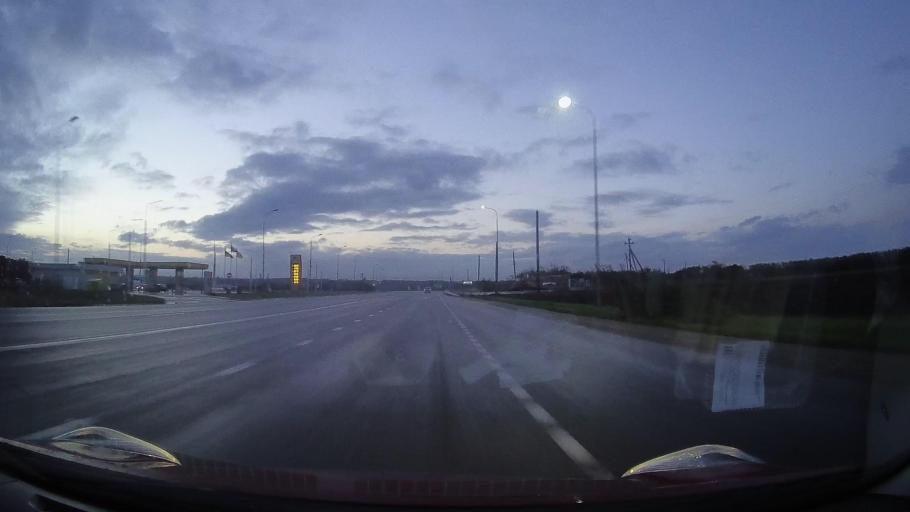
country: RU
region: Krasnodarskiy
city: Zavetnyy
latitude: 44.9093
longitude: 41.1663
